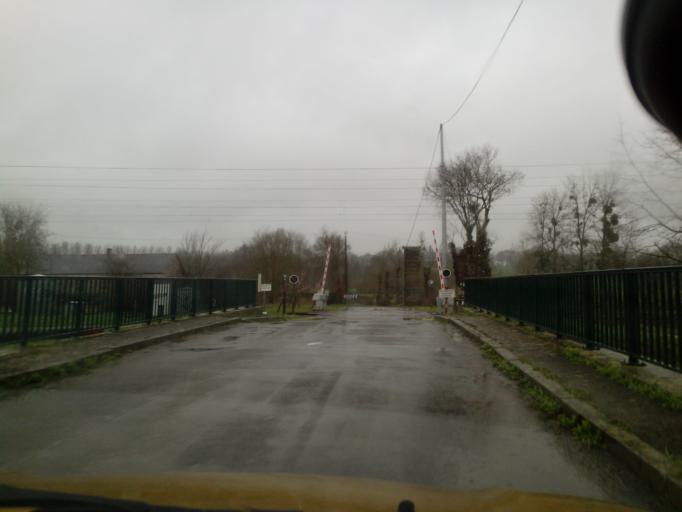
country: FR
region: Brittany
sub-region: Departement d'Ille-et-Vilaine
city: Chevaigne
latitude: 48.2363
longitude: -1.6490
